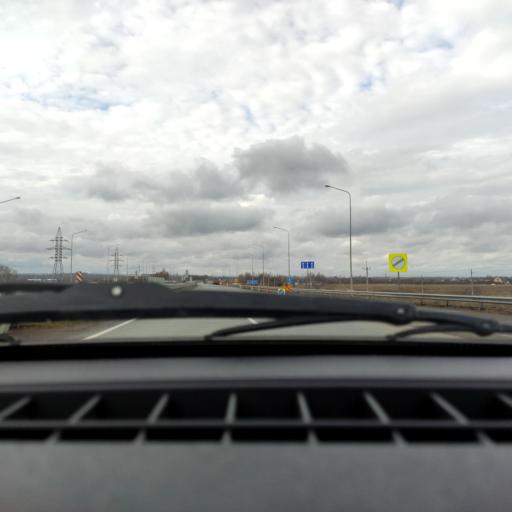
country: RU
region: Bashkortostan
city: Asanovo
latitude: 54.9043
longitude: 55.6224
